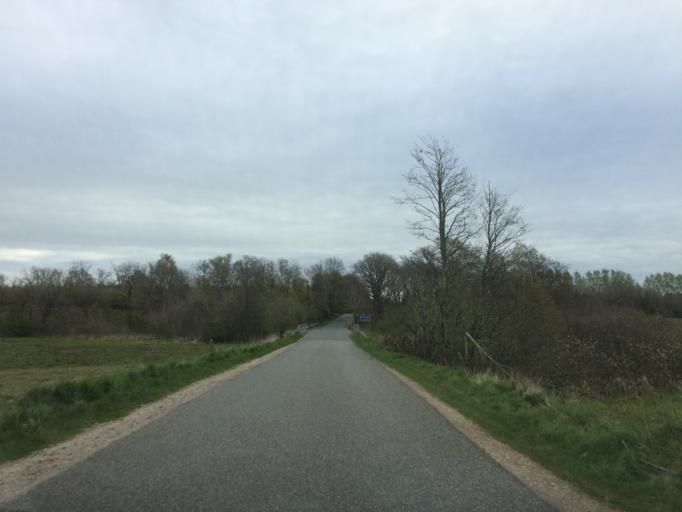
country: DK
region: Central Jutland
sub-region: Viborg Kommune
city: Karup
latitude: 56.3466
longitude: 9.1046
